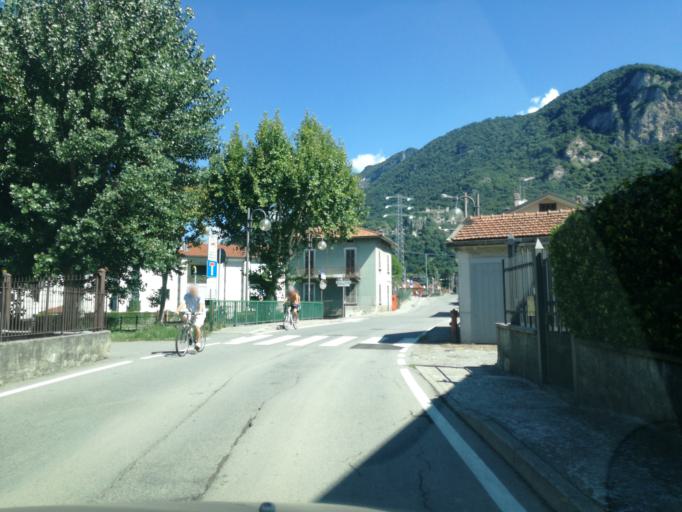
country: IT
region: Lombardy
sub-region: Provincia di Lecco
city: Vercurago
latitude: 45.8063
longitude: 9.4197
